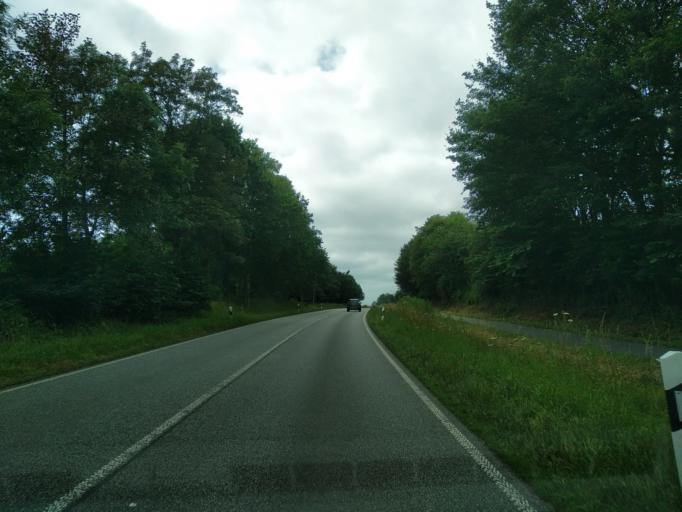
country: DE
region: Schleswig-Holstein
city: Wees
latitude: 54.8024
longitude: 9.5326
